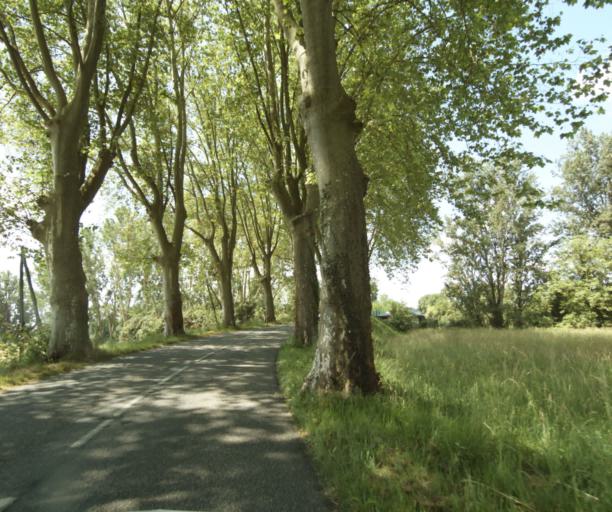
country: FR
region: Midi-Pyrenees
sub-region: Departement du Tarn-et-Garonne
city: Montauban
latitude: 44.0841
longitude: 1.3487
